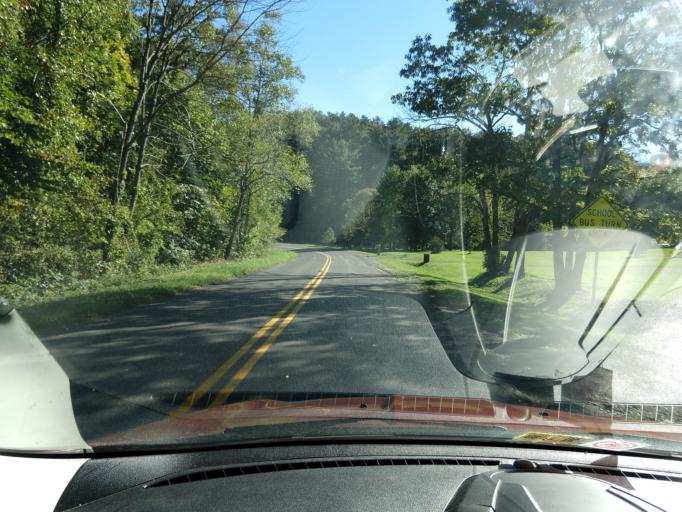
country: US
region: Virginia
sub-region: Alleghany County
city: Clifton Forge
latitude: 37.8416
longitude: -79.8493
